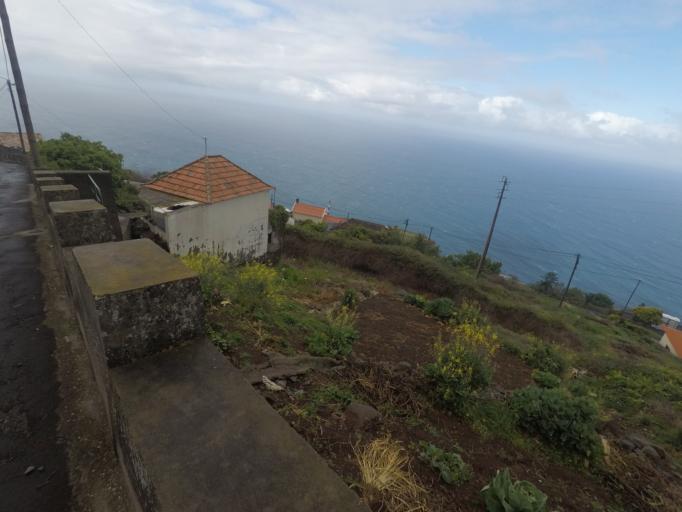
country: PT
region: Madeira
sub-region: Calheta
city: Faja da Ovelha
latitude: 32.7733
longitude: -17.2362
